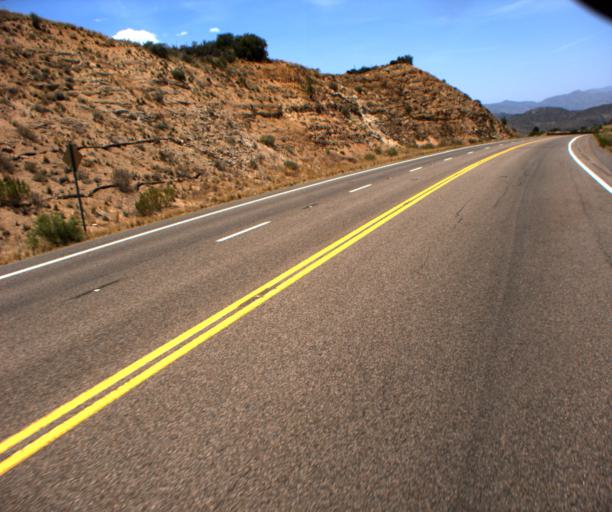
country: US
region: Arizona
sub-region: Gila County
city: Miami
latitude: 33.5368
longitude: -110.9307
